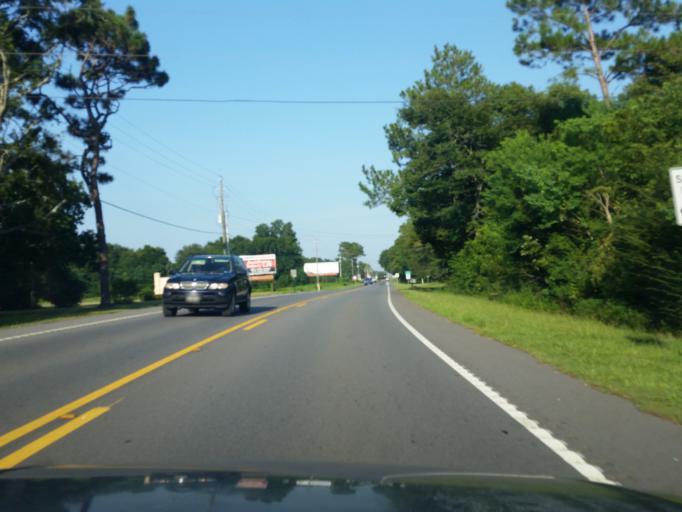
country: US
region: Alabama
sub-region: Baldwin County
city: Elberta
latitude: 30.4143
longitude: -87.6079
